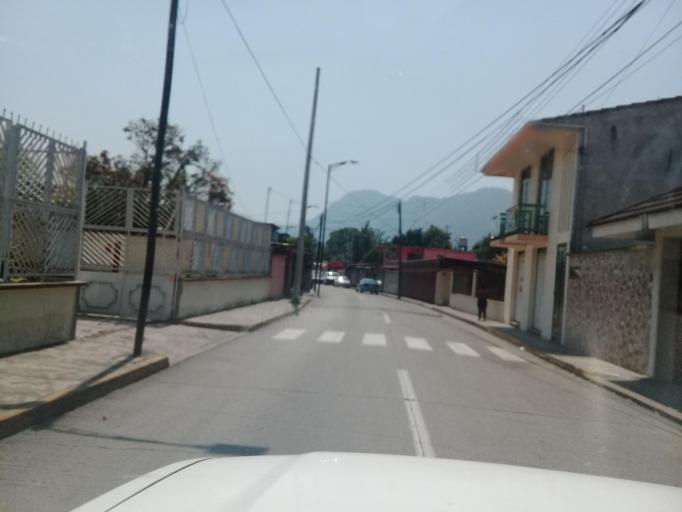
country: MX
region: Veracruz
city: Ixtac Zoquitlan
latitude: 18.8594
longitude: -97.0649
